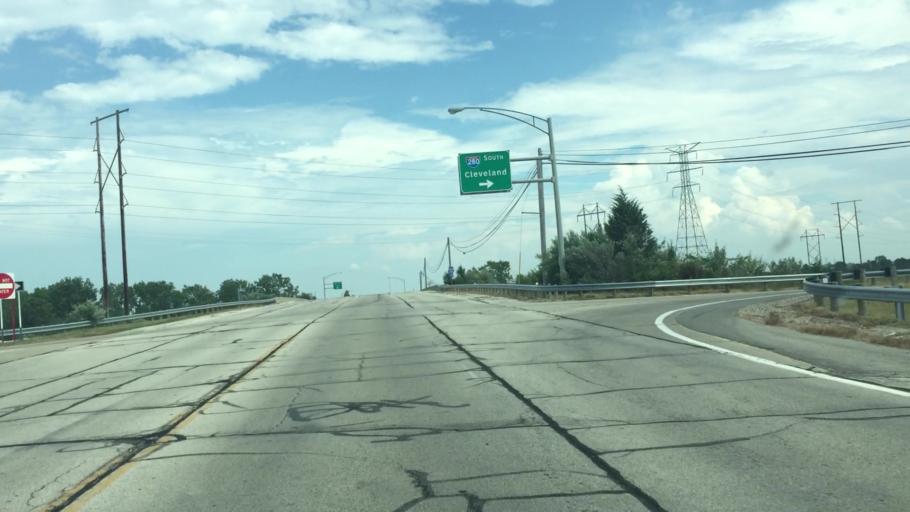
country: US
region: Ohio
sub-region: Wood County
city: Walbridge
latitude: 41.5879
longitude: -83.4788
